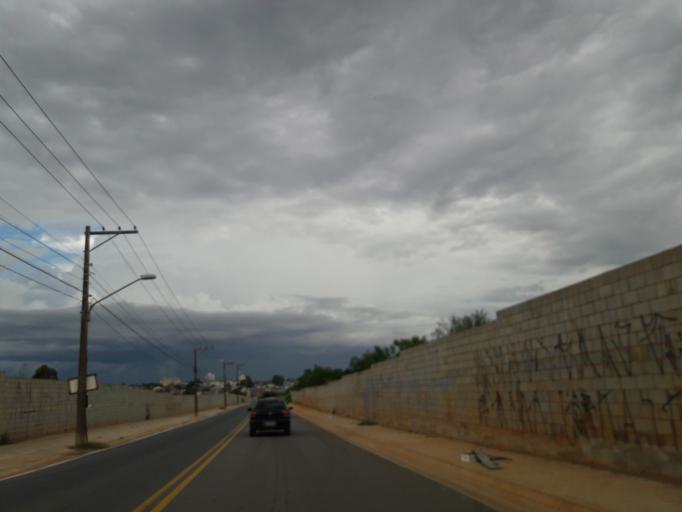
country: BR
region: Sao Paulo
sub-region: Aruja
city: Aruja
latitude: -23.3950
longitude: -46.4087
